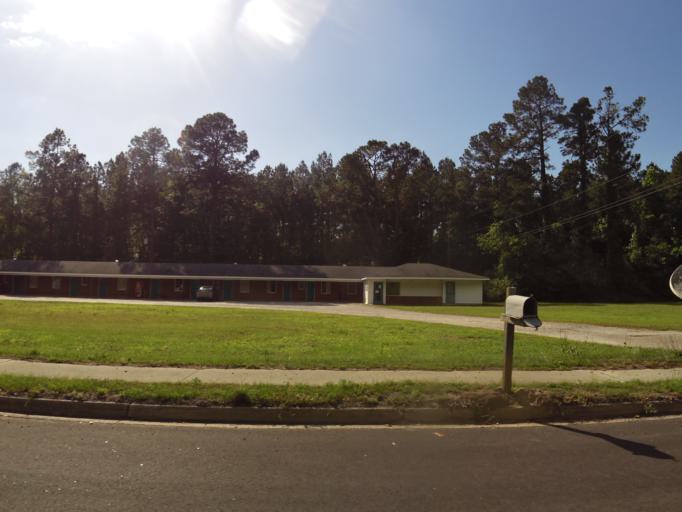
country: US
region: South Carolina
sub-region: Allendale County
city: Fairfax
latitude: 32.9724
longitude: -81.2321
